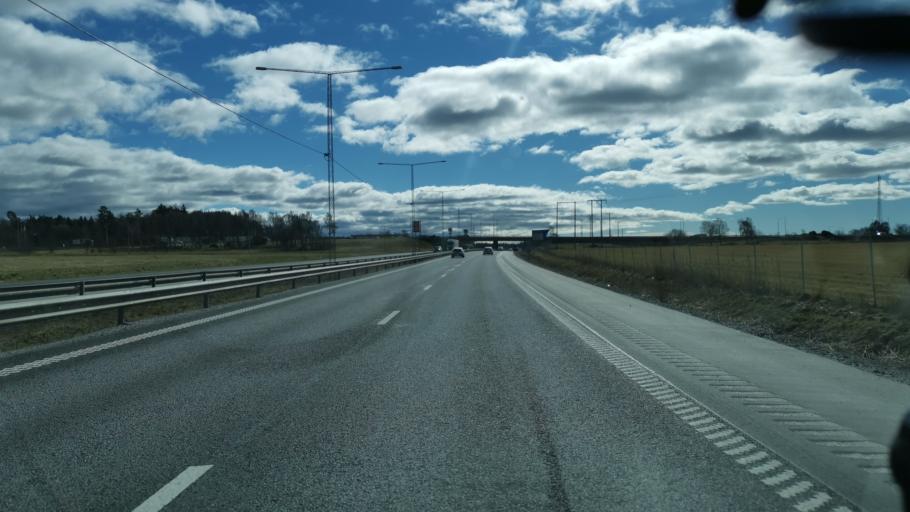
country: SE
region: Vaestra Goetaland
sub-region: Stenungsunds Kommun
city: Stora Hoga
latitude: 58.0284
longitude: 11.8463
